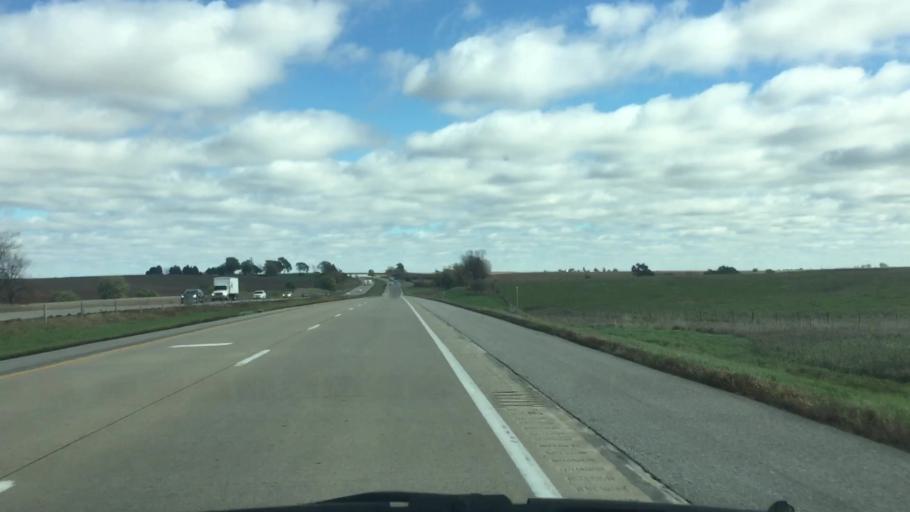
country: US
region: Iowa
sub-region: Poweshiek County
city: Brooklyn
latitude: 41.6952
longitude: -92.5171
